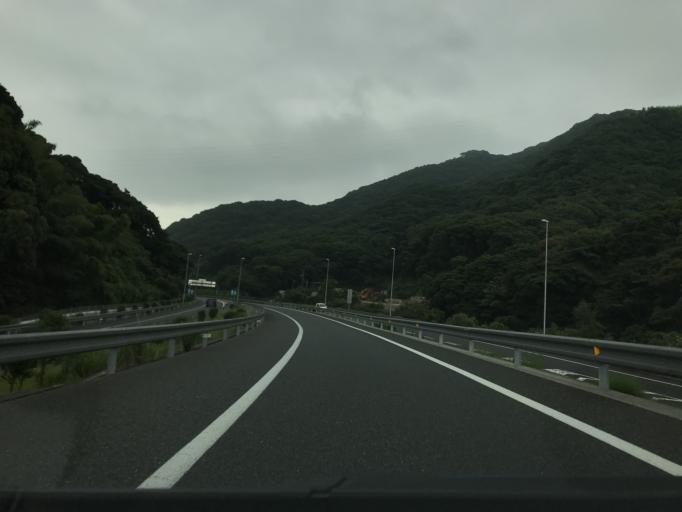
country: JP
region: Fukuoka
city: Kitakyushu
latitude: 33.8149
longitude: 130.8883
